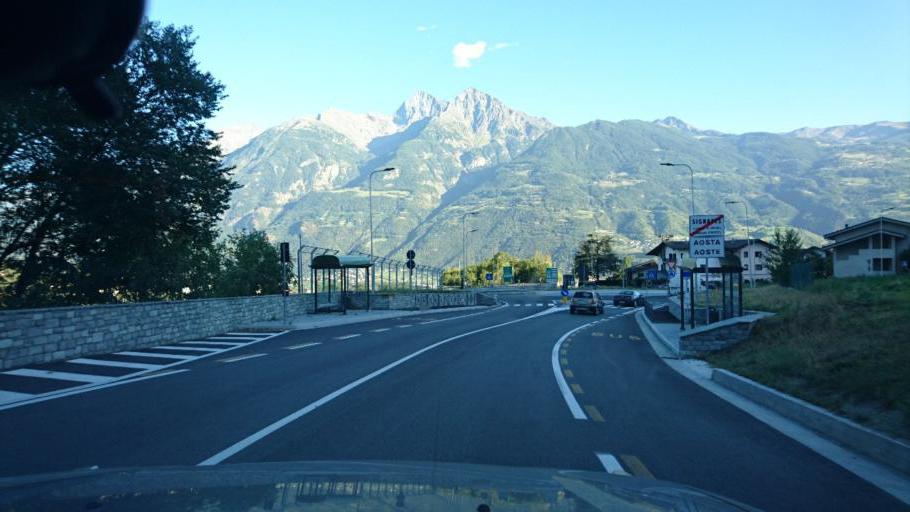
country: IT
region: Aosta Valley
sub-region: Valle d'Aosta
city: Aosta
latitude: 45.7512
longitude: 7.3183
